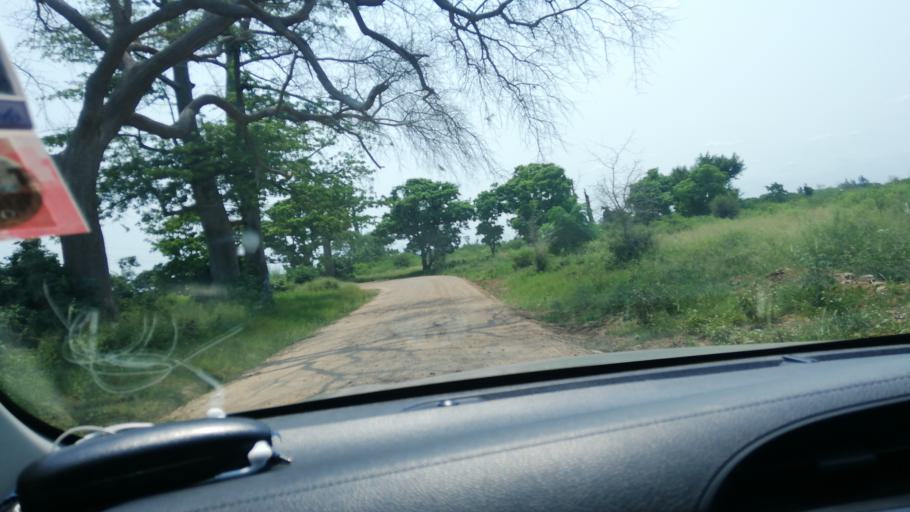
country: MZ
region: Maputo
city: Matola
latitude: -26.0572
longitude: 32.3882
